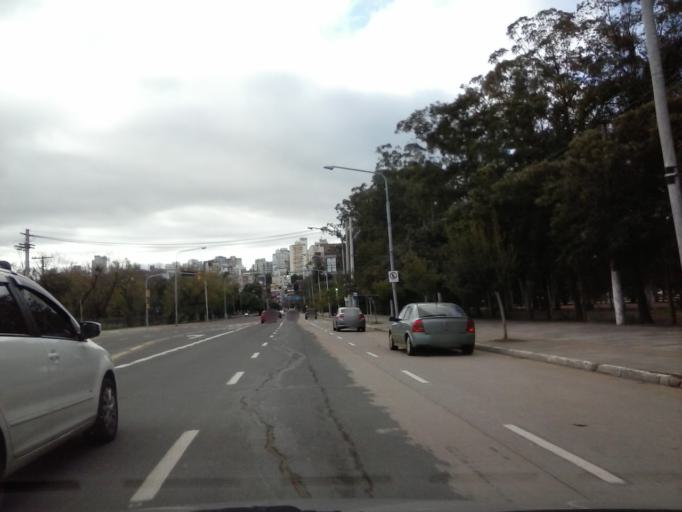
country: BR
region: Rio Grande do Sul
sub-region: Porto Alegre
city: Porto Alegre
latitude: -30.0410
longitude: -51.2330
